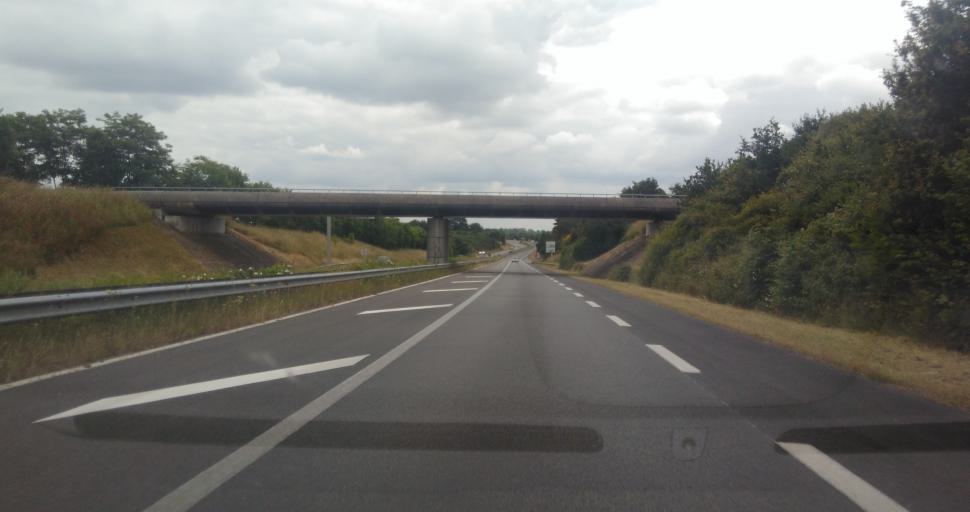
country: FR
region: Pays de la Loire
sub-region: Departement de la Vendee
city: Bournezeau
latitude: 46.6297
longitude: -1.1728
